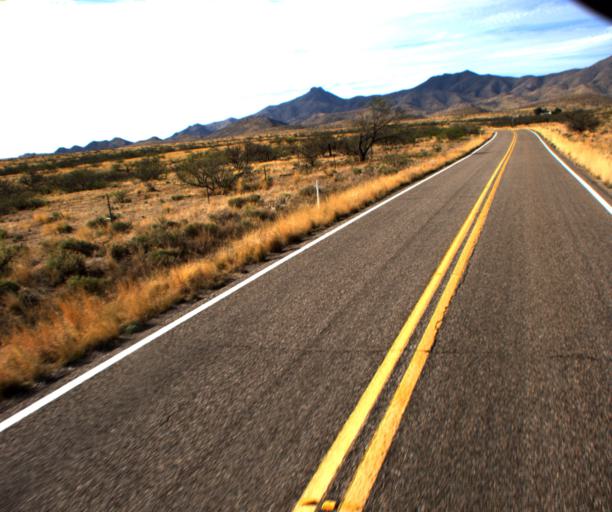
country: US
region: Arizona
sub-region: Cochise County
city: Willcox
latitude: 32.1238
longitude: -109.5559
